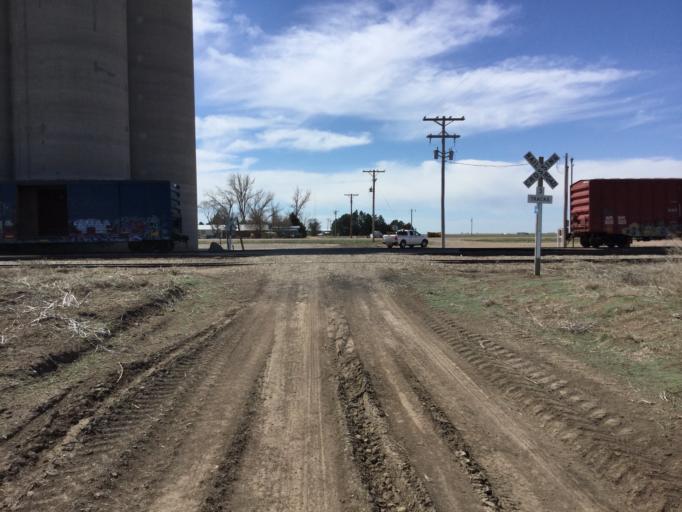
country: US
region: Kansas
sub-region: Sherman County
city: Goodland
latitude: 39.3402
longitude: -101.5495
